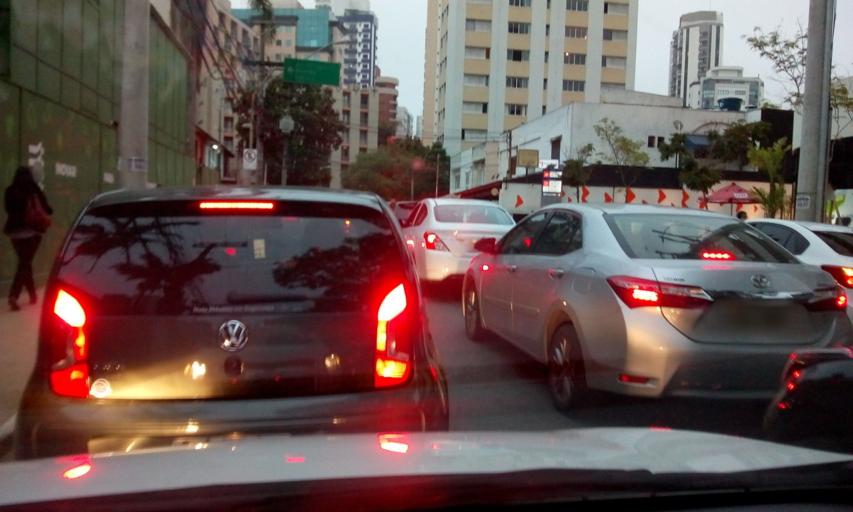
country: BR
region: Sao Paulo
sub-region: Sao Paulo
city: Sao Paulo
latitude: -23.6006
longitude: -46.6751
